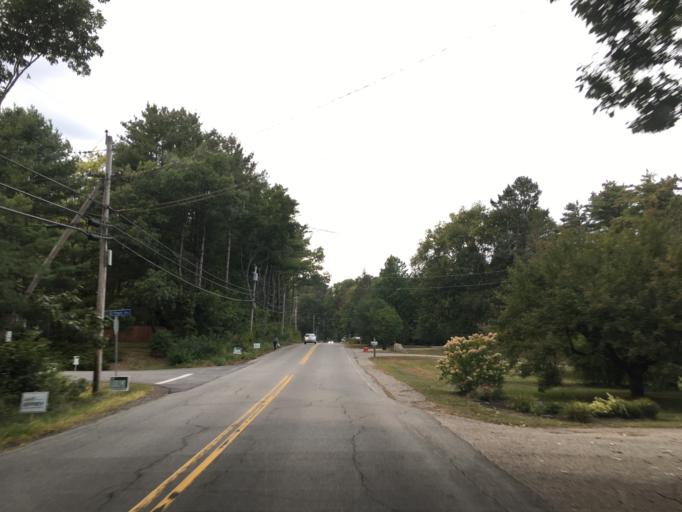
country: US
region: New Hampshire
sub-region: Rockingham County
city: Stratham Station
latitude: 43.0085
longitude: -70.9086
